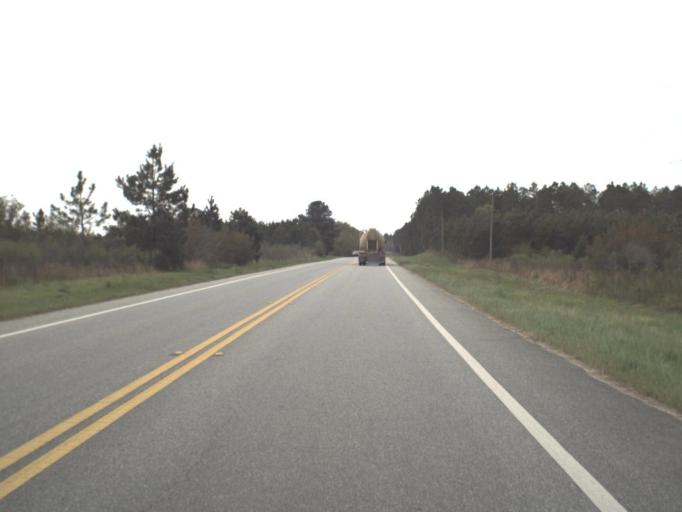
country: US
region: Florida
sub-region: Holmes County
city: Bonifay
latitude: 30.9026
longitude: -85.6525
